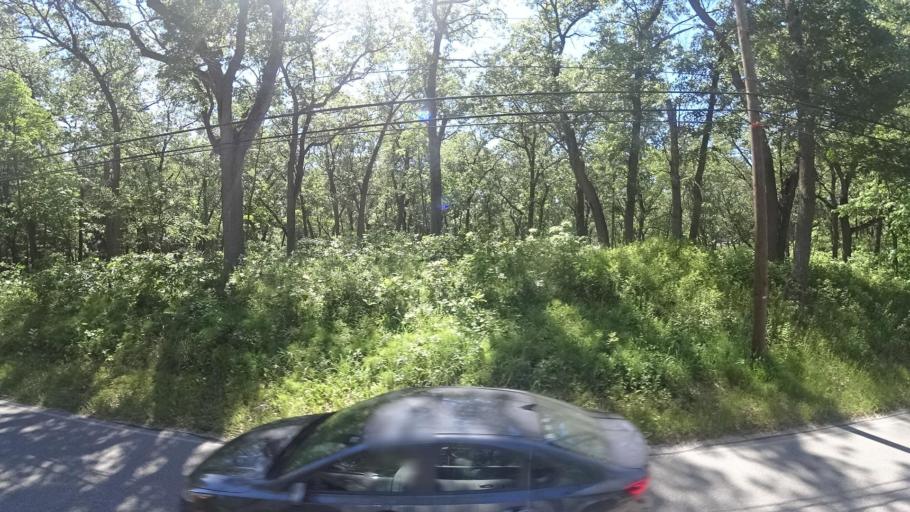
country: US
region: Indiana
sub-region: Porter County
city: Porter
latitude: 41.6538
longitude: -87.0674
